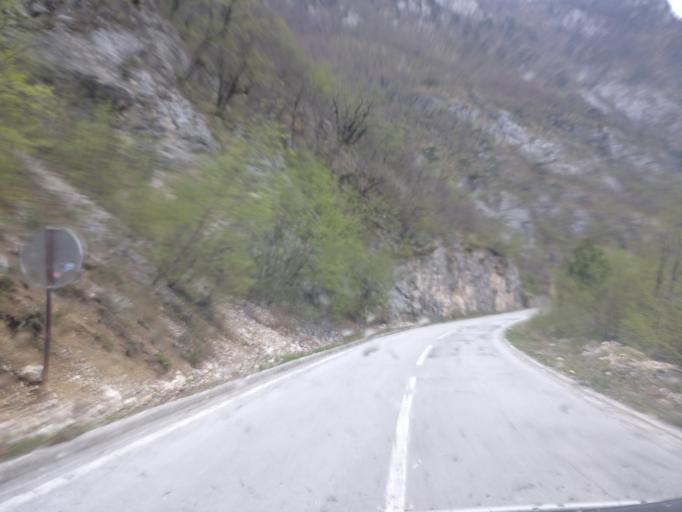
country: ME
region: Opstina Pluzine
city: Pluzine
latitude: 43.2122
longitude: 18.8582
